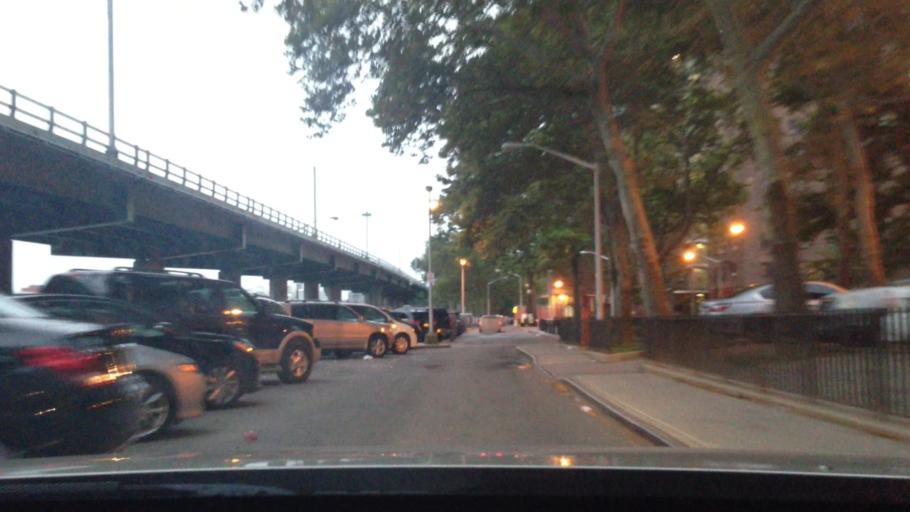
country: US
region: New York
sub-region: New York County
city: Inwood
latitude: 40.8332
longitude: -73.9356
